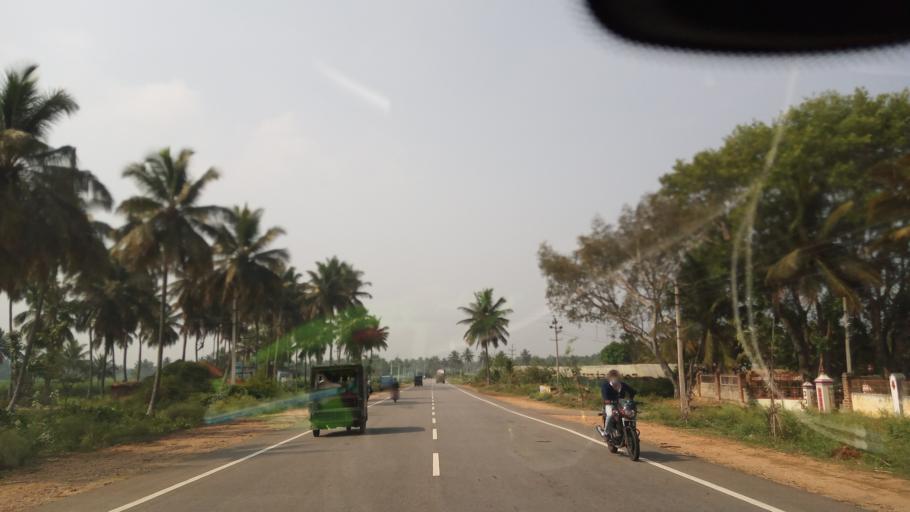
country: IN
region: Karnataka
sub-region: Mandya
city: Pandavapura
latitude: 12.5466
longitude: 76.6712
